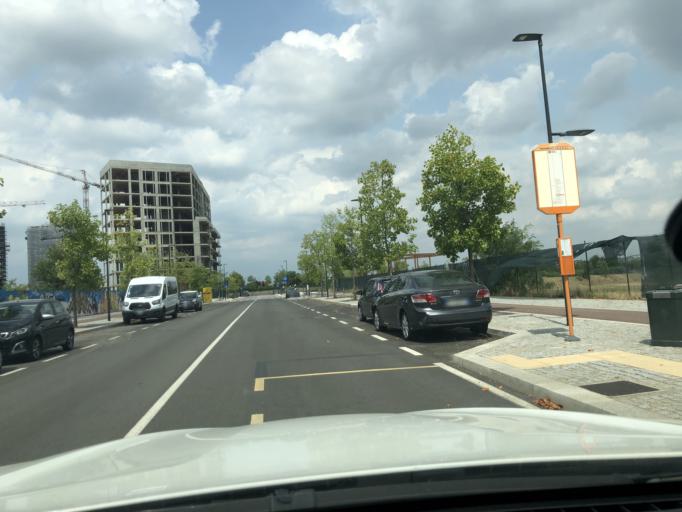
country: IT
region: Lombardy
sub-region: Citta metropolitana di Milano
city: Pero
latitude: 45.5093
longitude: 9.1013
